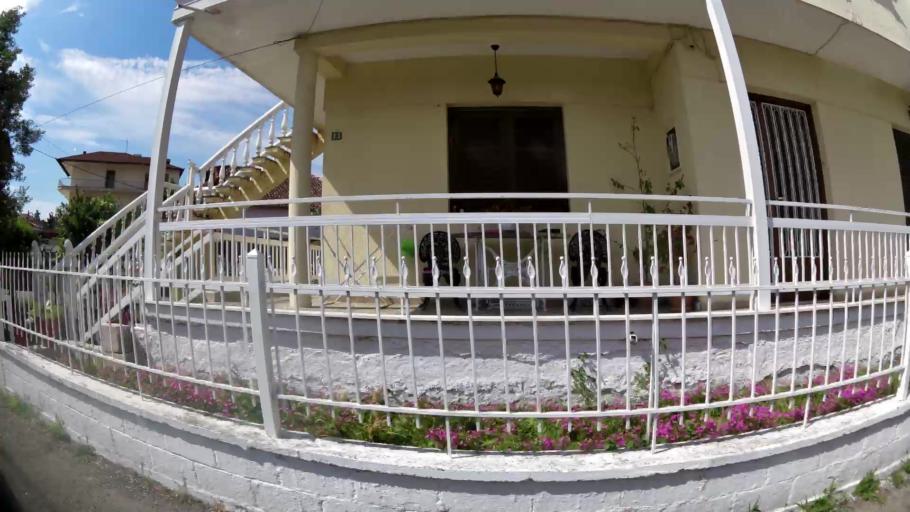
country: GR
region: Central Macedonia
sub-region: Nomos Pierias
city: Katerini
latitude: 40.2731
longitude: 22.4876
